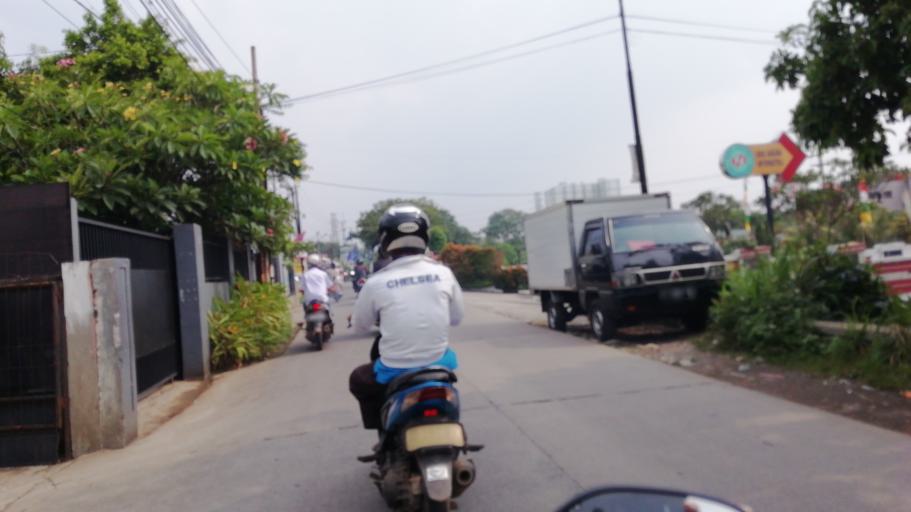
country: ID
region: West Java
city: Bogor
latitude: -6.5553
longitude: 106.8005
